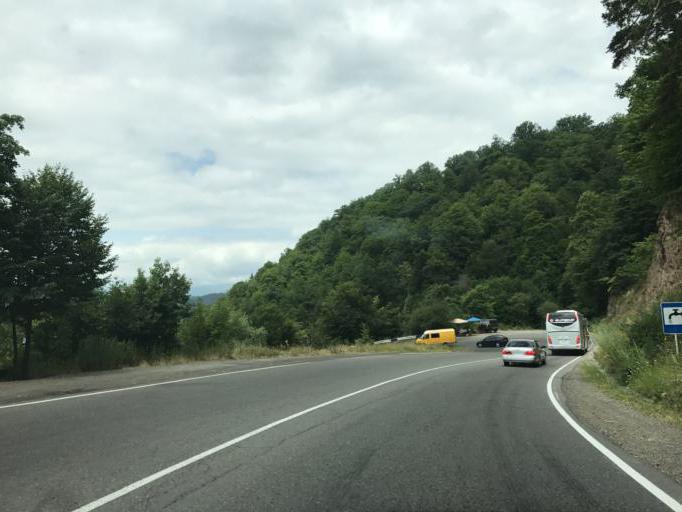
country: AM
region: Tavush
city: Dilijan
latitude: 40.6924
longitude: 44.8600
